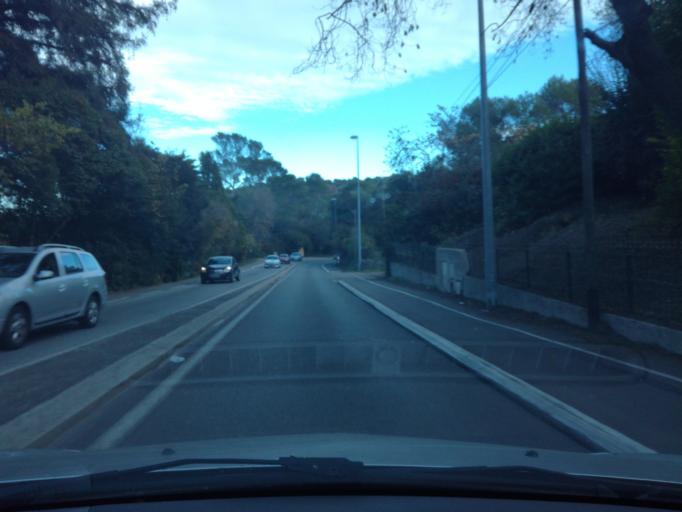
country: FR
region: Provence-Alpes-Cote d'Azur
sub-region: Departement des Alpes-Maritimes
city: Mougins
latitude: 43.6032
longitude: 7.0241
